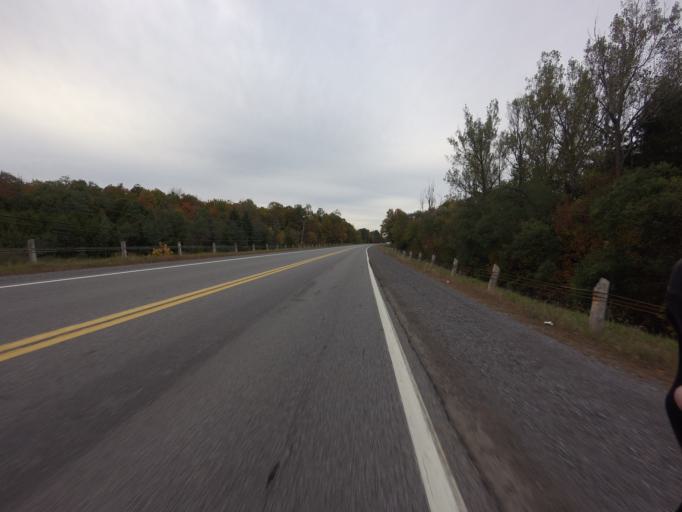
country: CA
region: Ontario
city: Bells Corners
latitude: 45.1512
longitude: -75.7109
